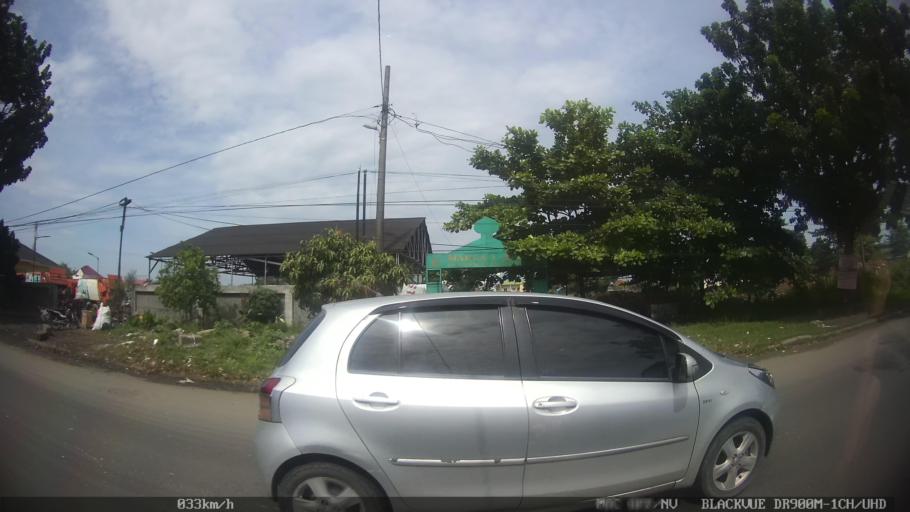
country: ID
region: North Sumatra
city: Sunggal
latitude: 3.6086
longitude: 98.6276
